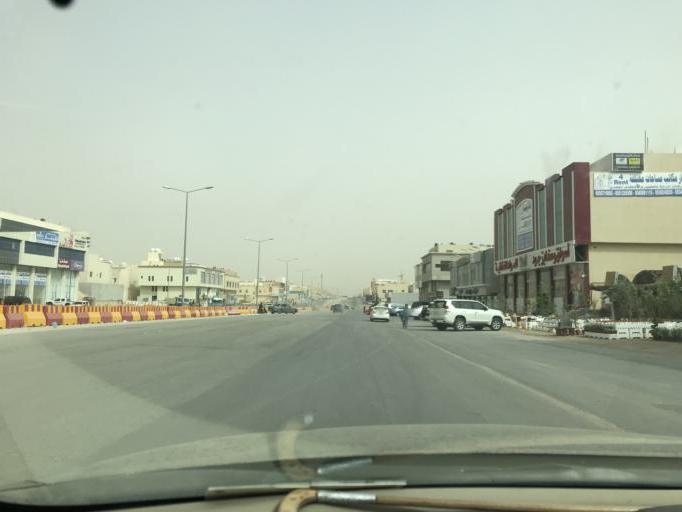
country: SA
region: Ar Riyad
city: Riyadh
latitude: 24.8130
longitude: 46.5994
